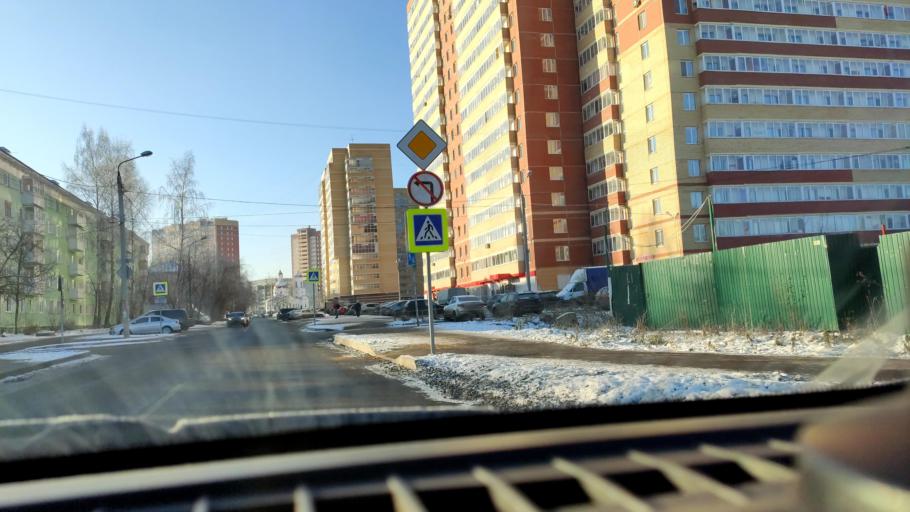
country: RU
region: Perm
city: Kondratovo
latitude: 58.0509
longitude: 56.0913
